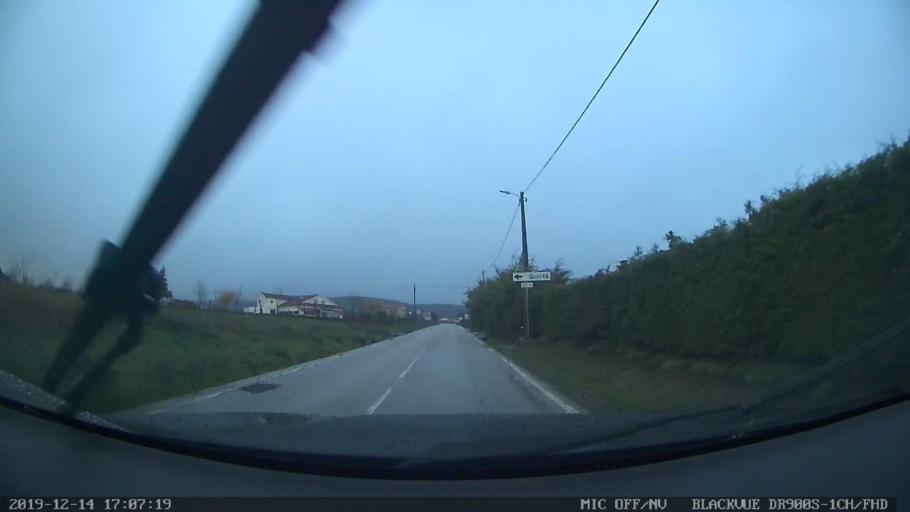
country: PT
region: Vila Real
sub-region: Vila Pouca de Aguiar
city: Vila Pouca de Aguiar
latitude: 41.4609
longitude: -7.5974
